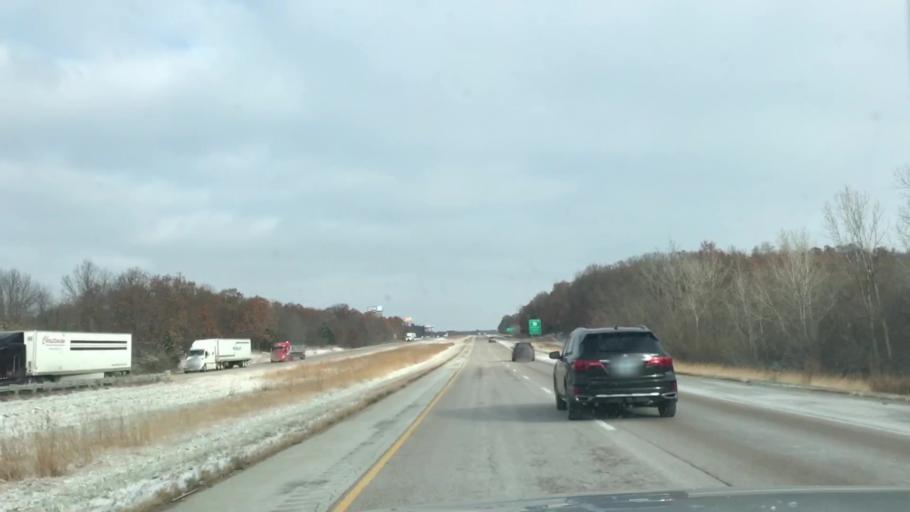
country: US
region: Illinois
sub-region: Macoupin County
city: Mount Olive
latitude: 39.0586
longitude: -89.7556
